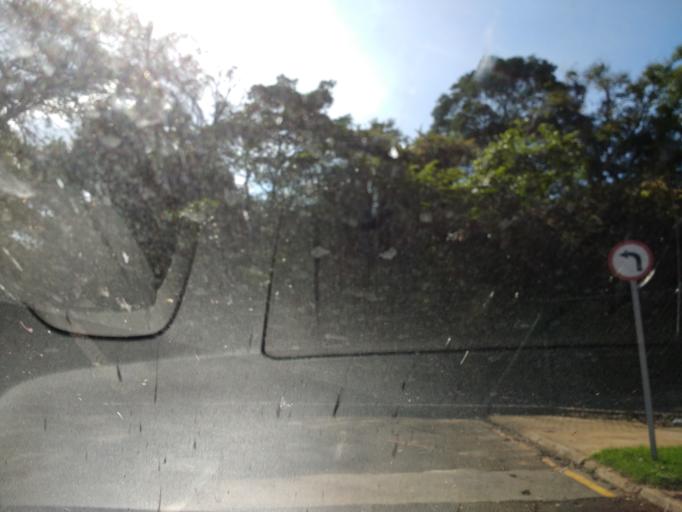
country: BR
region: Parana
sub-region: Maringa
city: Maringa
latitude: -23.4202
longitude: -51.9673
